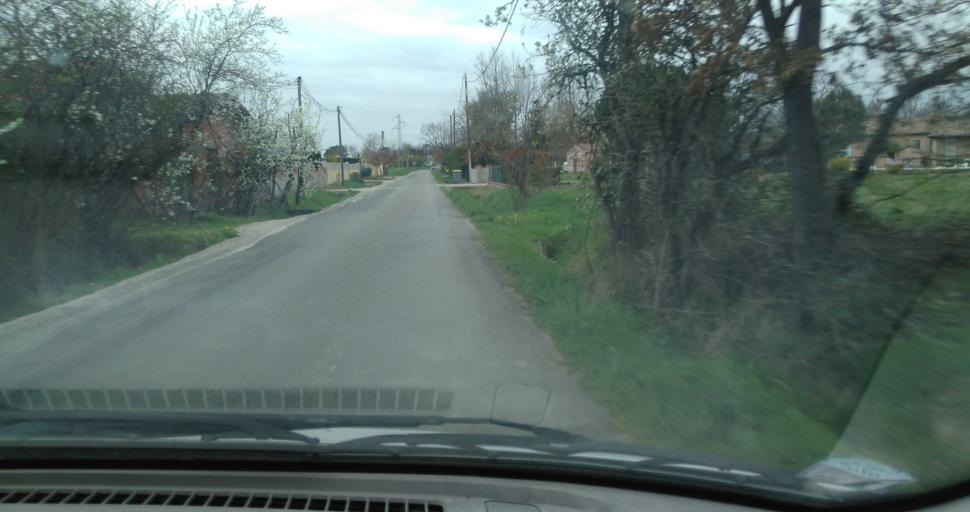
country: FR
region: Midi-Pyrenees
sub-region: Departement du Tarn-et-Garonne
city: Montbeton
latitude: 43.9979
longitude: 1.2786
